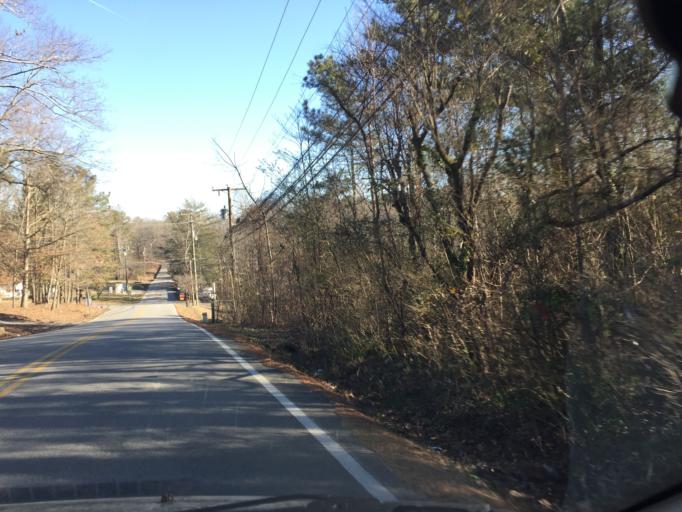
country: US
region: Tennessee
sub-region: Hamilton County
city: Collegedale
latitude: 35.0440
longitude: -85.0989
